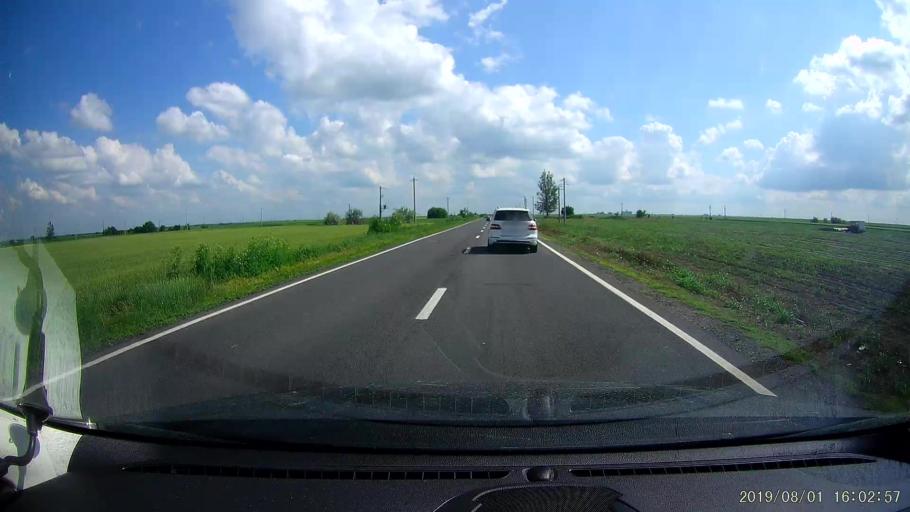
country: RO
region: Calarasi
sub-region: Comuna Dragalina
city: Drajna Noua
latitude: 44.4810
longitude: 27.3859
